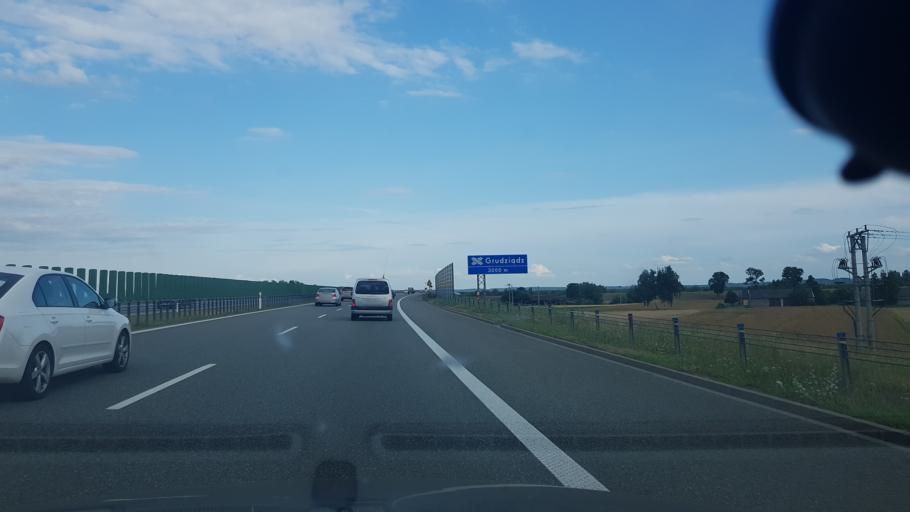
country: PL
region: Kujawsko-Pomorskie
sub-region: Grudziadz
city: Grudziadz
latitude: 53.4509
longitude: 18.6668
